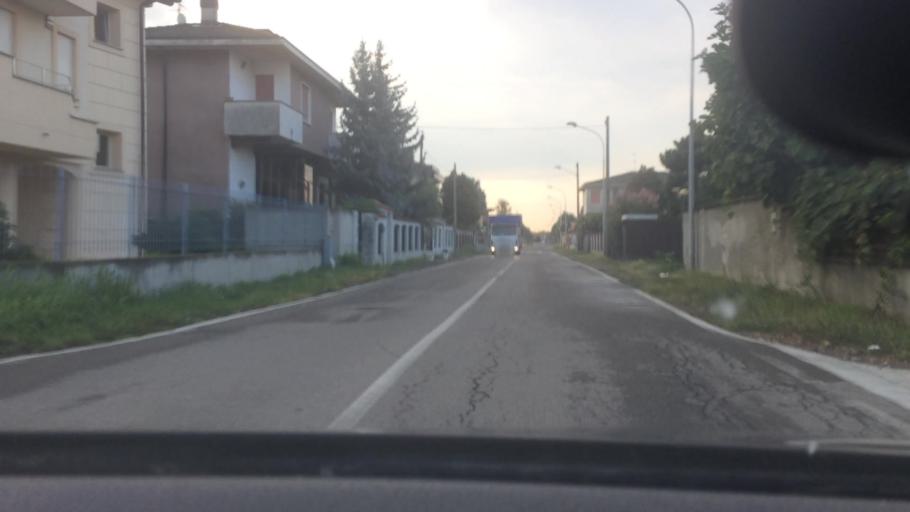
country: IT
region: Lombardy
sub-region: Citta metropolitana di Milano
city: Busto Garolfo
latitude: 45.5489
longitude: 8.8917
